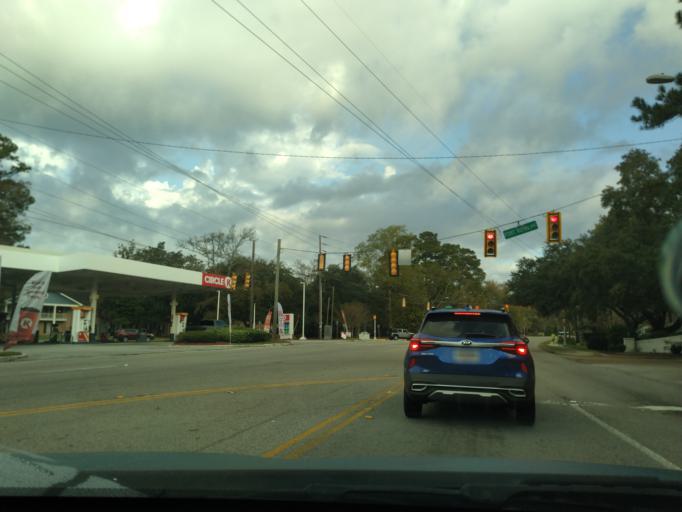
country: US
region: South Carolina
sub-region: Charleston County
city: North Charleston
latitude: 32.7985
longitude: -79.9960
